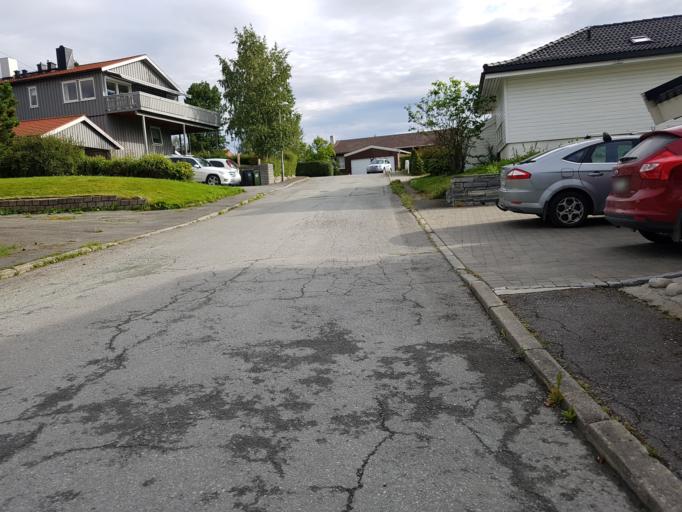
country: NO
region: Sor-Trondelag
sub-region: Trondheim
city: Trondheim
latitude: 63.3885
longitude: 10.4223
